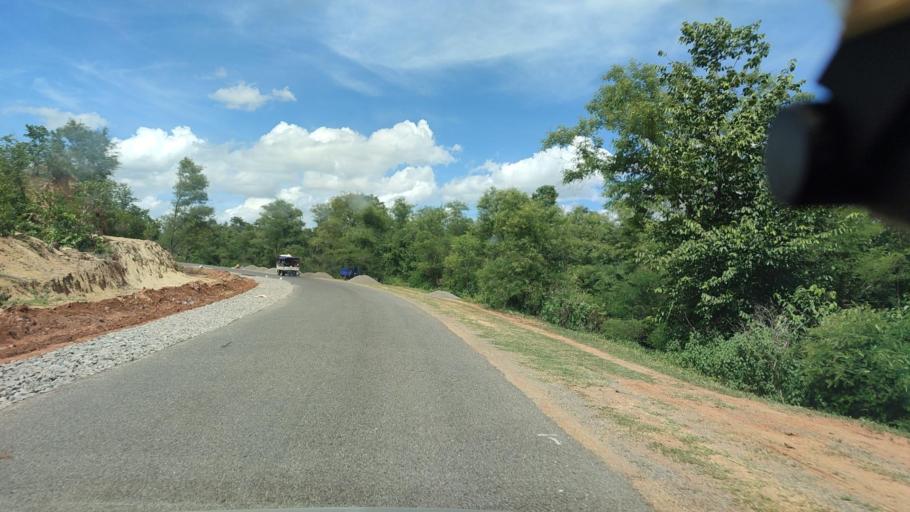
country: MM
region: Magway
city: Magway
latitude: 20.1888
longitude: 95.1949
